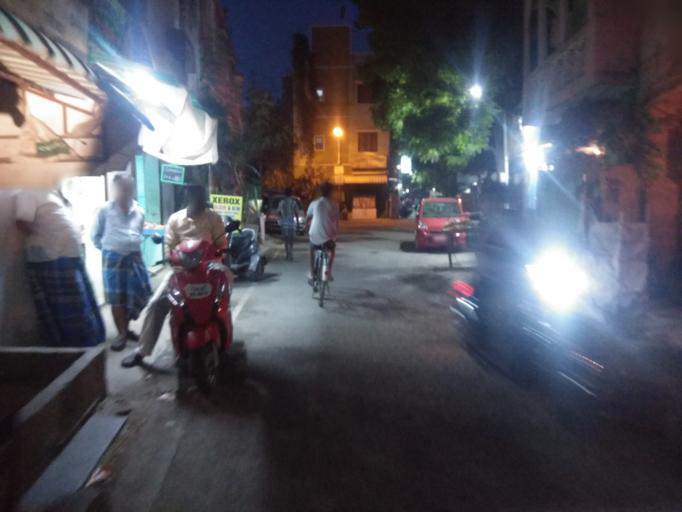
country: IN
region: Tamil Nadu
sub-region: Chennai
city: Chetput
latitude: 13.0664
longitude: 80.2161
